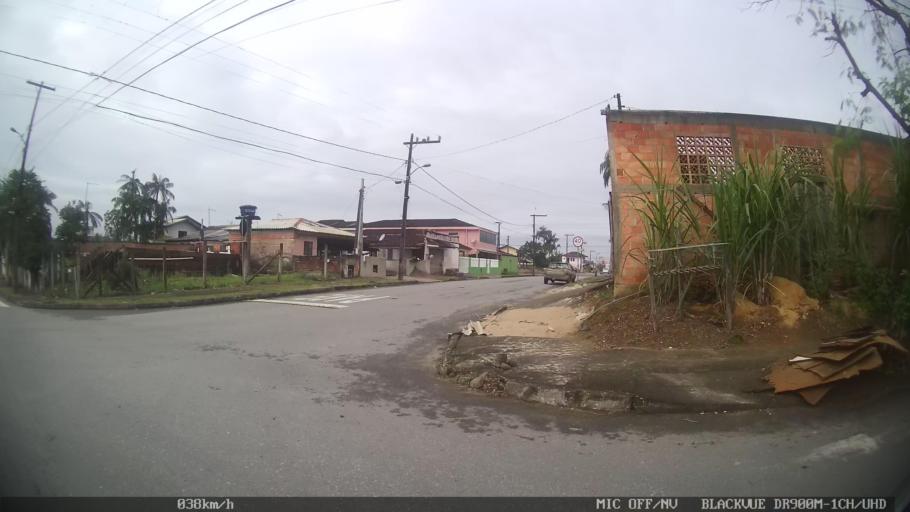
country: BR
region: Santa Catarina
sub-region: Joinville
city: Joinville
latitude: -26.0333
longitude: -48.8504
